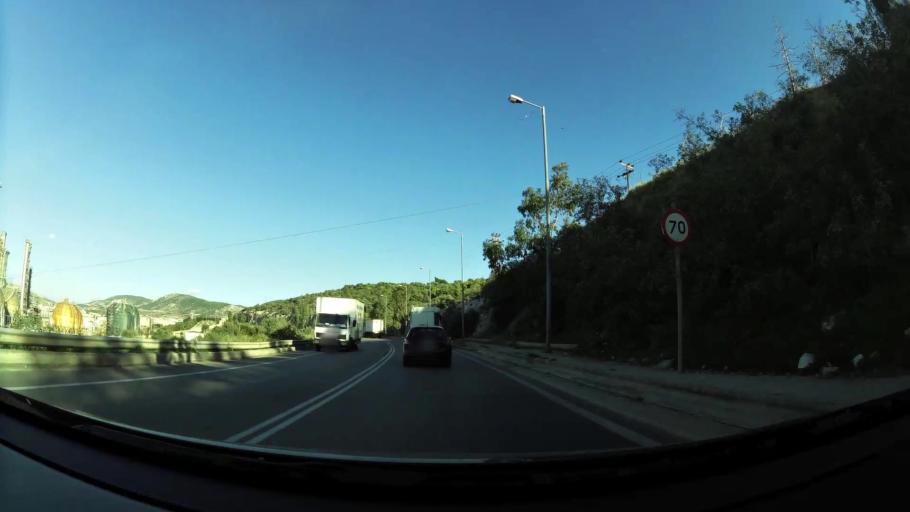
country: GR
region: Attica
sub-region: Nomarchia Athinas
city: Skaramangas
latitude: 38.0276
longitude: 23.6028
